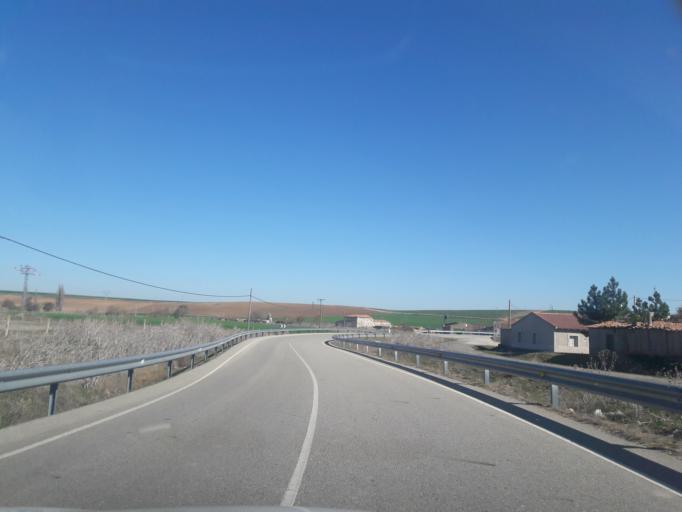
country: ES
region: Castille and Leon
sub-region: Provincia de Salamanca
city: Mancera de Abajo
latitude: 40.8373
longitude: -5.2025
